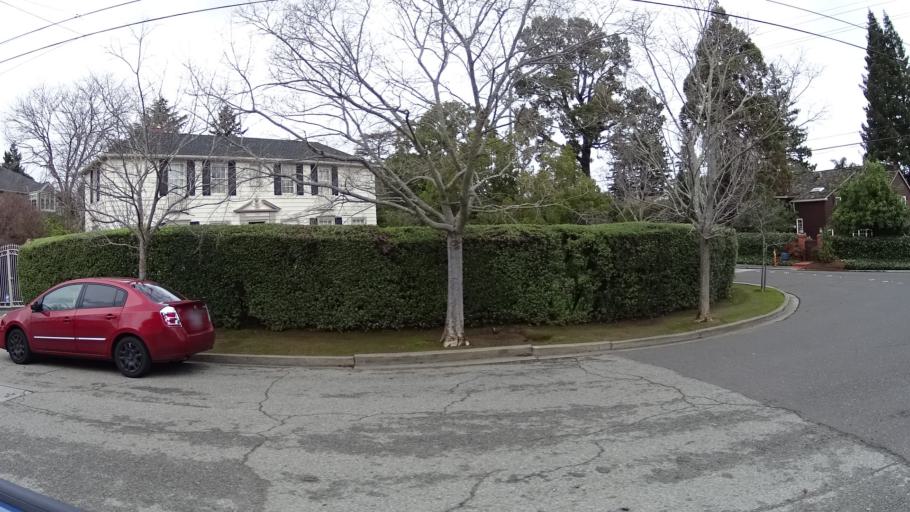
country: US
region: California
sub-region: San Mateo County
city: San Mateo
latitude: 37.5705
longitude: -122.3414
